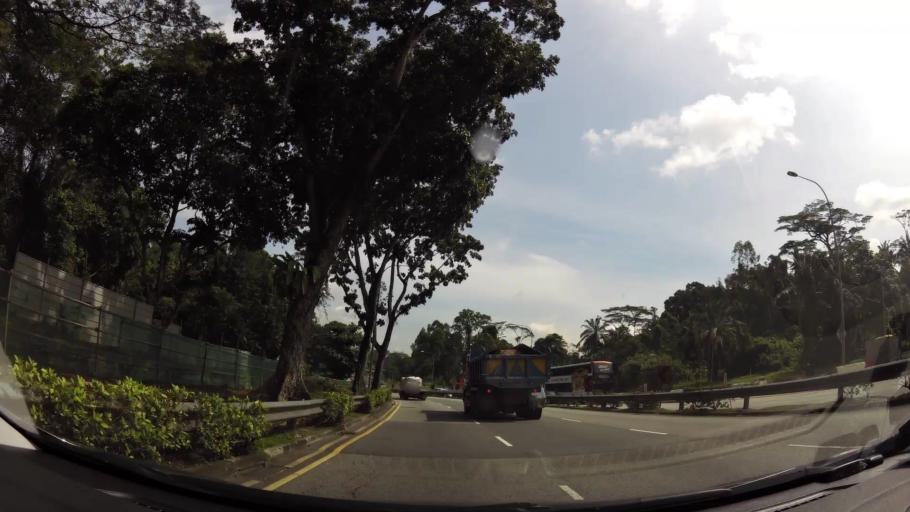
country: SG
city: Singapore
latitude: 1.3256
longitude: 103.7749
